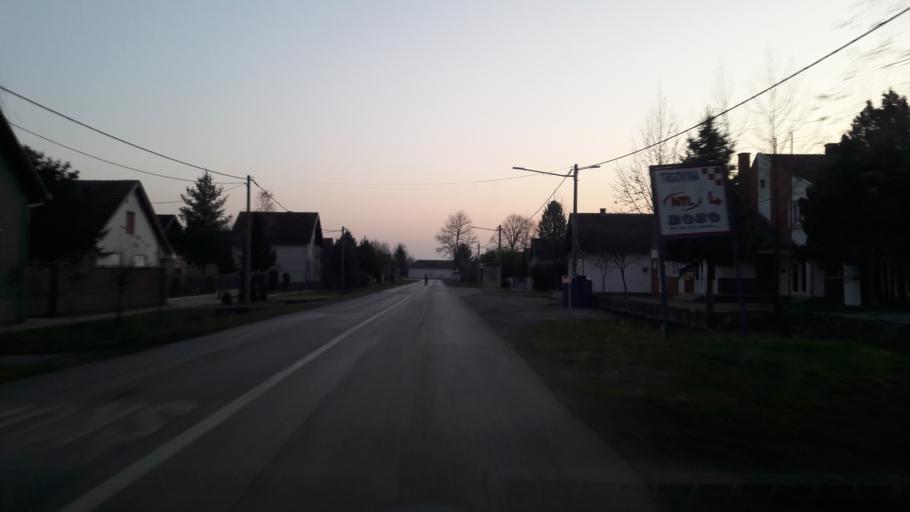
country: HR
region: Vukovarsko-Srijemska
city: Nijemci
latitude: 45.1815
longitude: 19.0123
